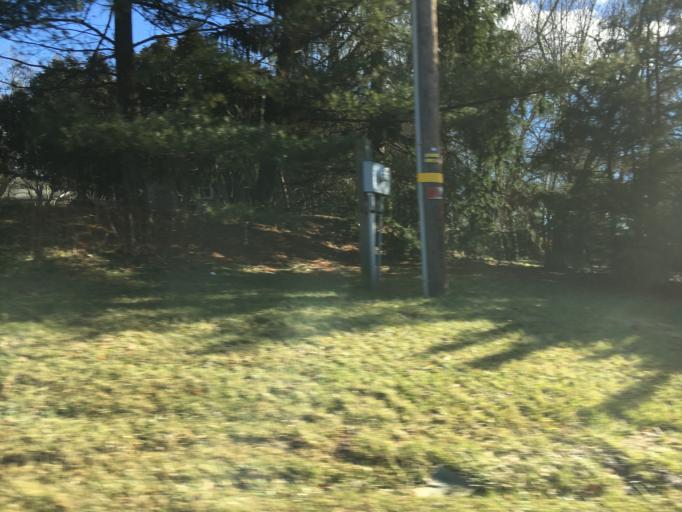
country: US
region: Pennsylvania
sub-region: Lehigh County
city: Allentown
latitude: 40.6307
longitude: -75.5088
